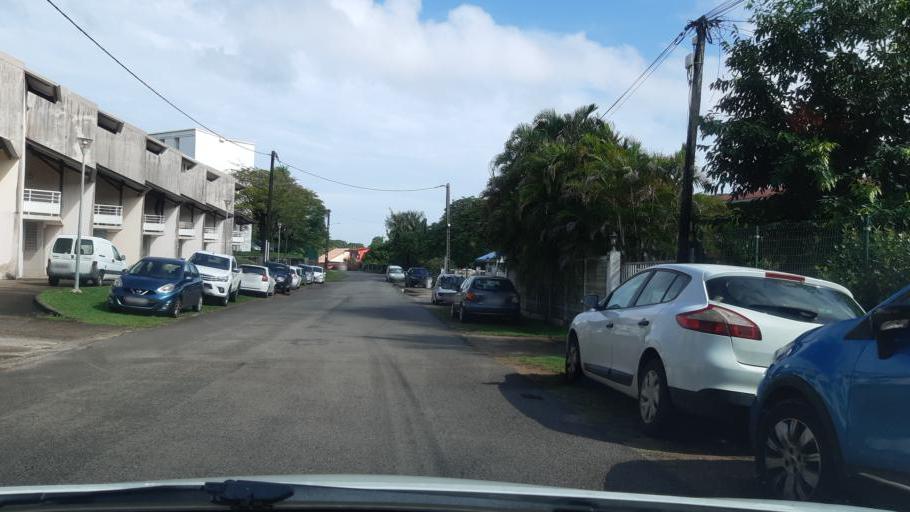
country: GF
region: Guyane
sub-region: Guyane
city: Cayenne
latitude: 4.9405
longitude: -52.3176
